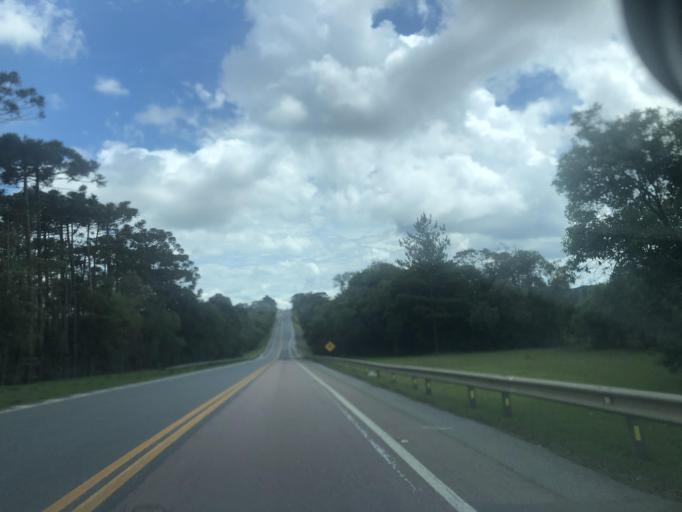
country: BR
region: Santa Catarina
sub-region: Mafra
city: Mafra
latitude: -26.1978
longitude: -49.8793
